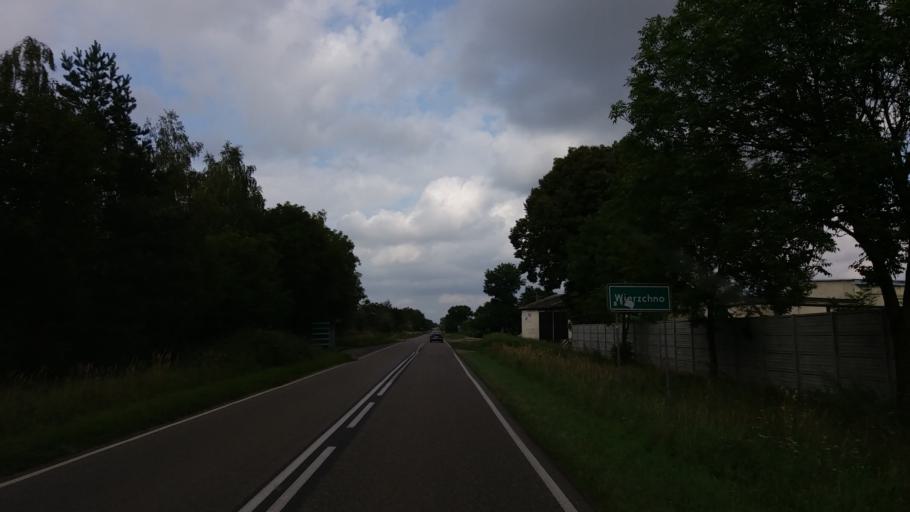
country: PL
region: West Pomeranian Voivodeship
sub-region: Powiat choszczenski
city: Pelczyce
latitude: 53.0154
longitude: 15.2693
